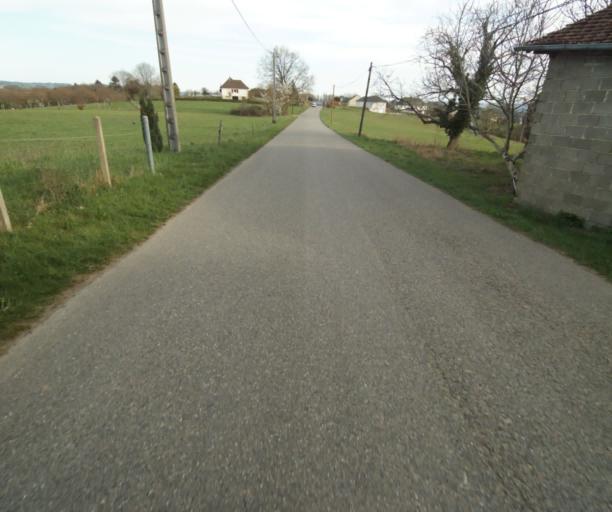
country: FR
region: Limousin
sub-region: Departement de la Correze
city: Naves
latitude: 45.3242
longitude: 1.7584
